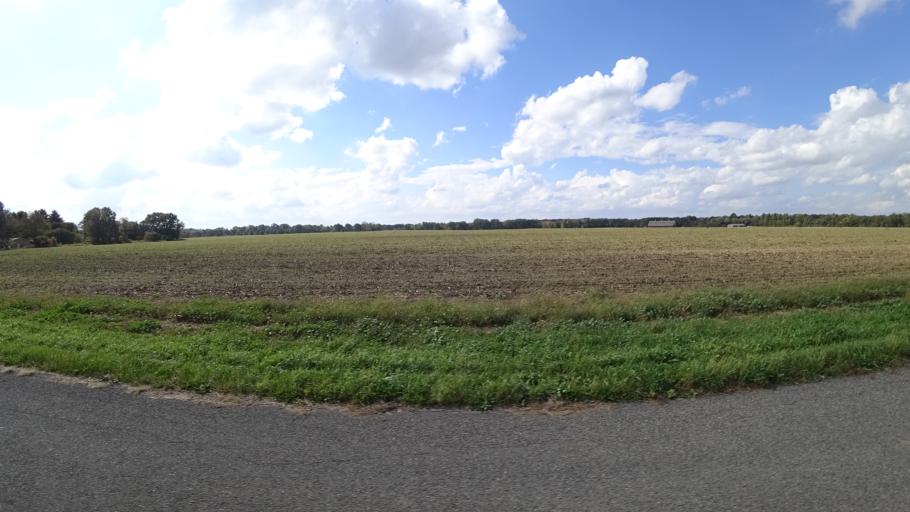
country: US
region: Michigan
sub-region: Saint Joseph County
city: Three Rivers
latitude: 41.9601
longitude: -85.6056
